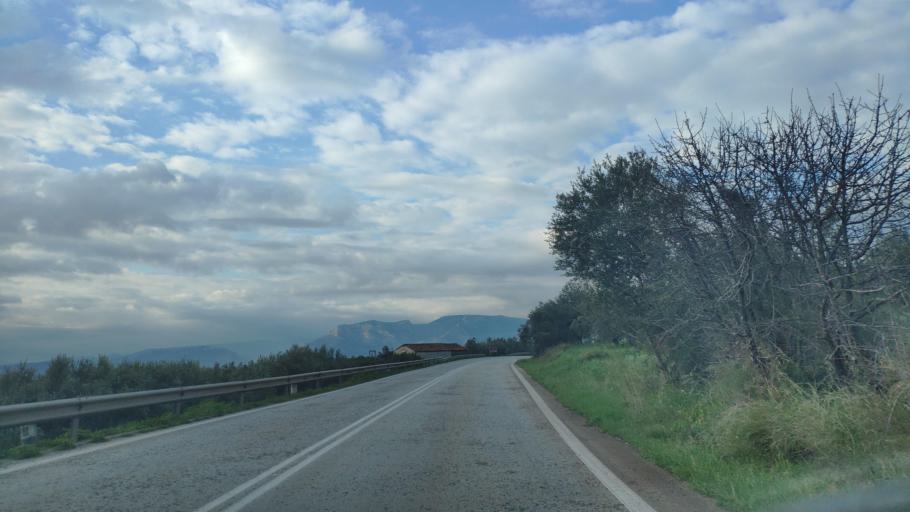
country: GR
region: Peloponnese
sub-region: Nomos Argolidos
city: Koutsopodi
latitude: 37.7308
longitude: 22.7339
